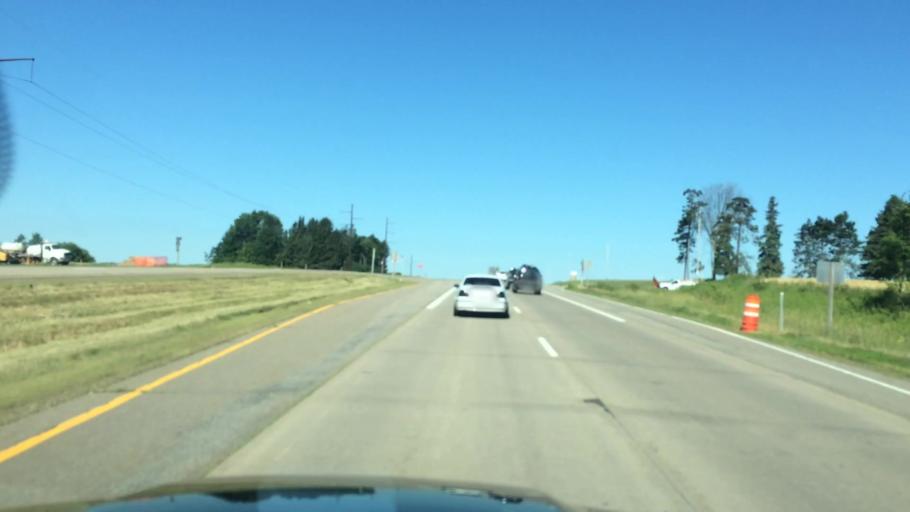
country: US
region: Wisconsin
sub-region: Marathon County
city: Edgar
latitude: 44.9446
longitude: -89.9244
